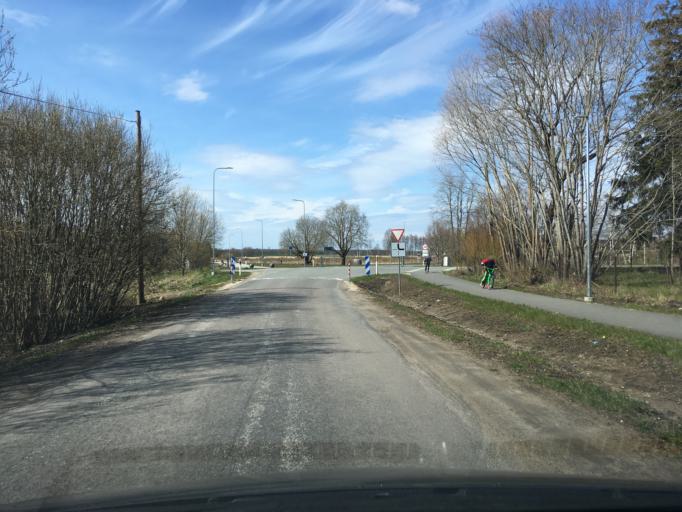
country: EE
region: Harju
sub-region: Raasiku vald
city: Raasiku
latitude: 59.3667
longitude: 25.1750
